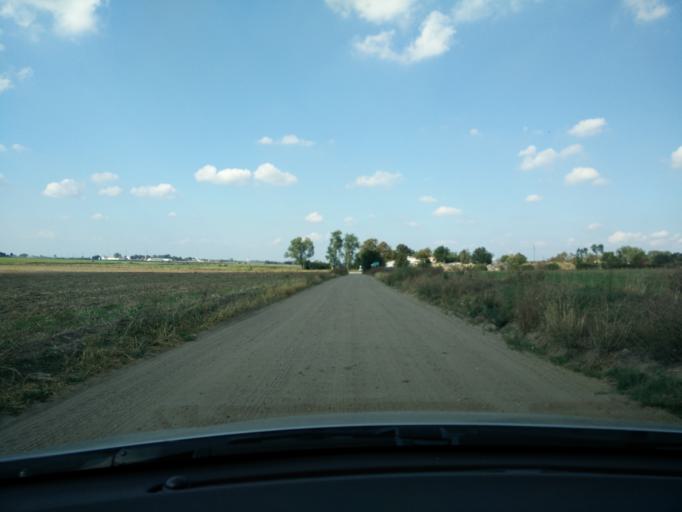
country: PL
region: Greater Poland Voivodeship
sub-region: Powiat poznanski
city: Kleszczewo
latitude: 52.2648
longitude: 17.1766
